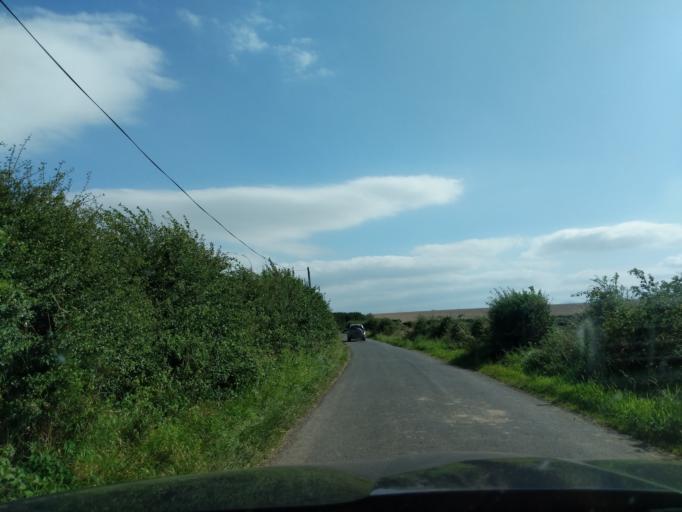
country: GB
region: Scotland
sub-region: The Scottish Borders
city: Coldstream
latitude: 55.6707
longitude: -2.1684
